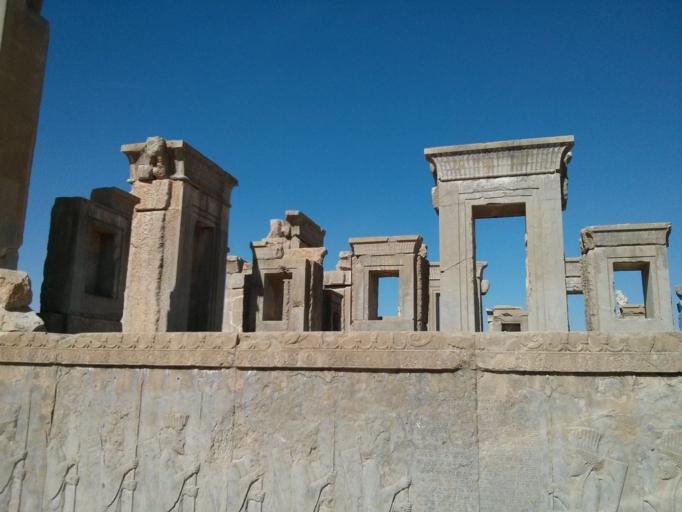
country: IR
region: Fars
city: Marvdasht
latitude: 29.9343
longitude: 52.8896
